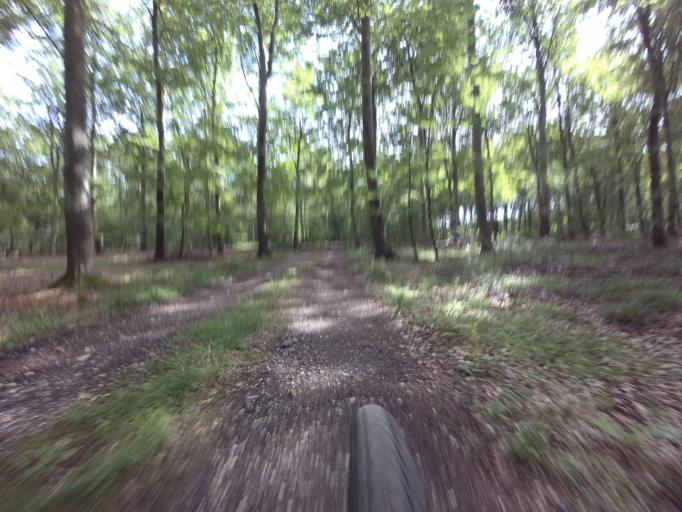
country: DK
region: Zealand
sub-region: Faxe Kommune
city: Fakse Ladeplads
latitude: 55.2338
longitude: 12.2030
